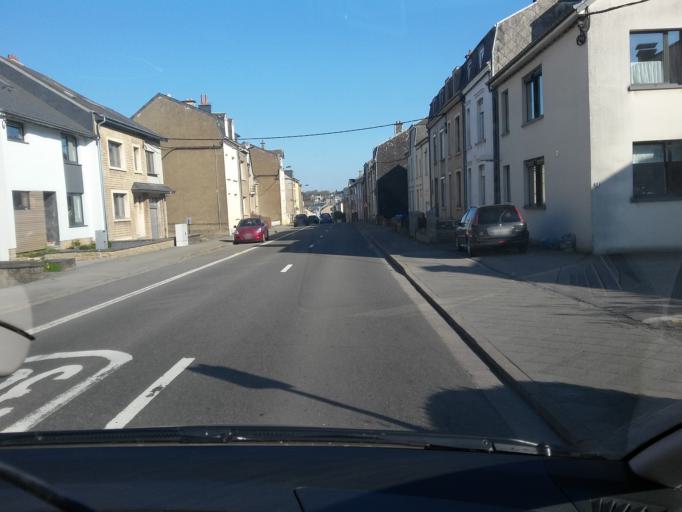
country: BE
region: Wallonia
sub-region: Province du Luxembourg
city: Arlon
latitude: 49.6735
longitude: 5.8148
